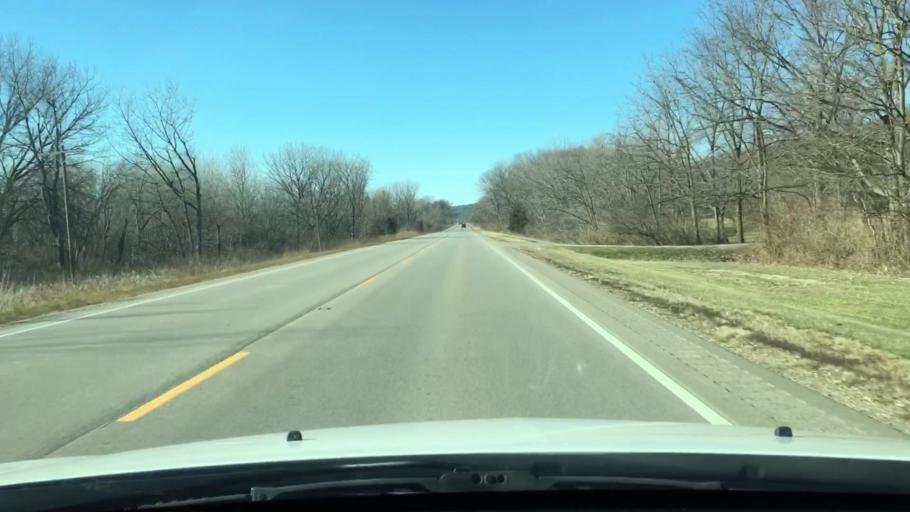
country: US
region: Illinois
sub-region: Peoria County
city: Glasford
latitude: 40.5508
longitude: -89.8239
